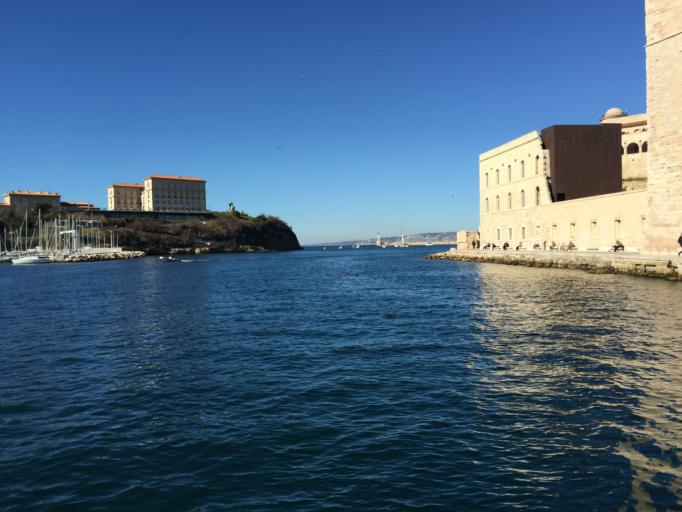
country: FR
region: Provence-Alpes-Cote d'Azur
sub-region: Departement des Bouches-du-Rhone
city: Marseille 02
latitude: 43.2943
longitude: 5.3633
